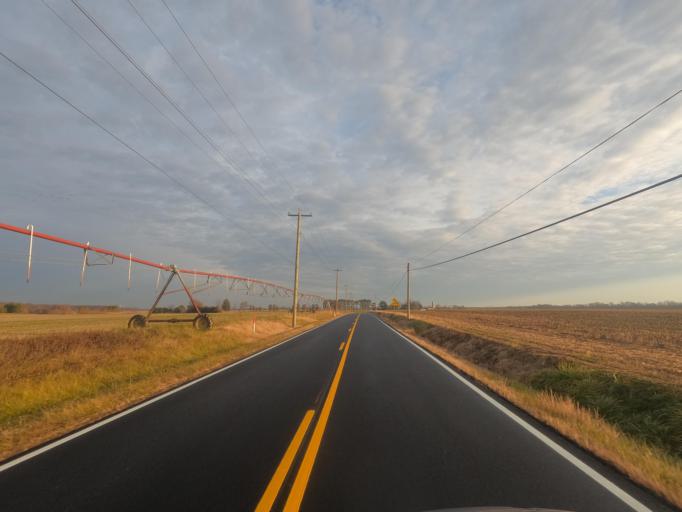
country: US
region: Delaware
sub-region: New Castle County
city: Townsend
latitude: 39.2880
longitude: -75.8341
